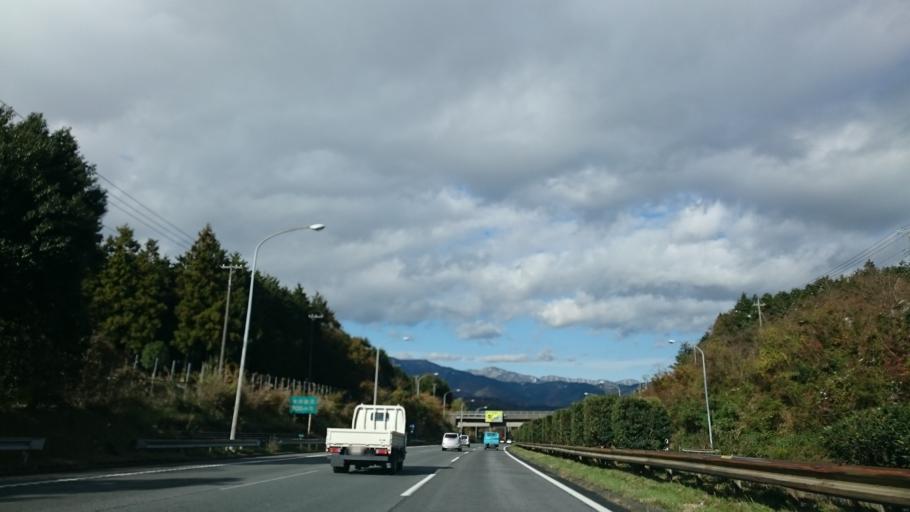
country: JP
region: Shizuoka
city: Gotemba
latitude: 35.3316
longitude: 138.9720
